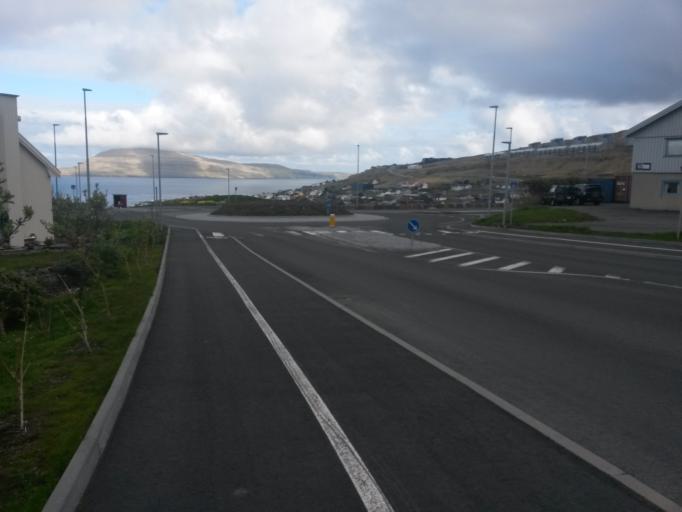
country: FO
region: Streymoy
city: Argir
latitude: 62.0007
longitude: -6.7970
